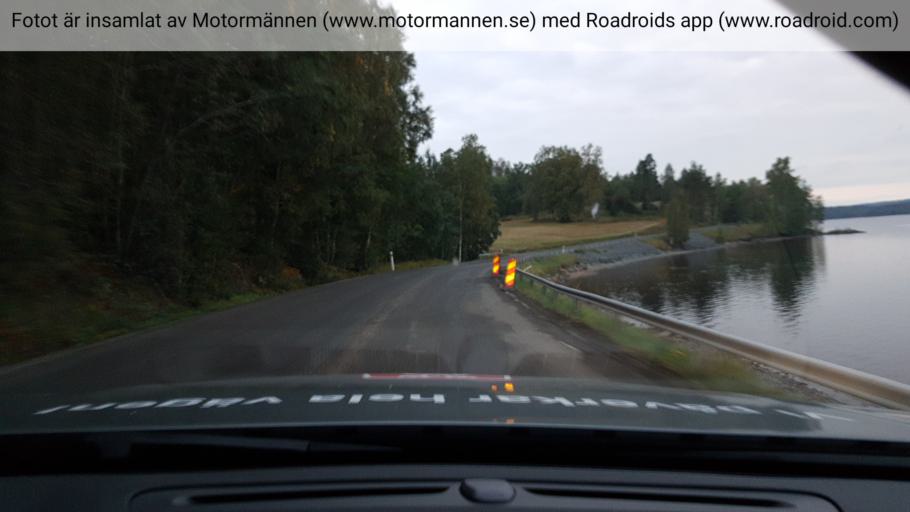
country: SE
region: OErebro
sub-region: Nora Kommun
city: As
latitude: 59.4901
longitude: 14.9404
